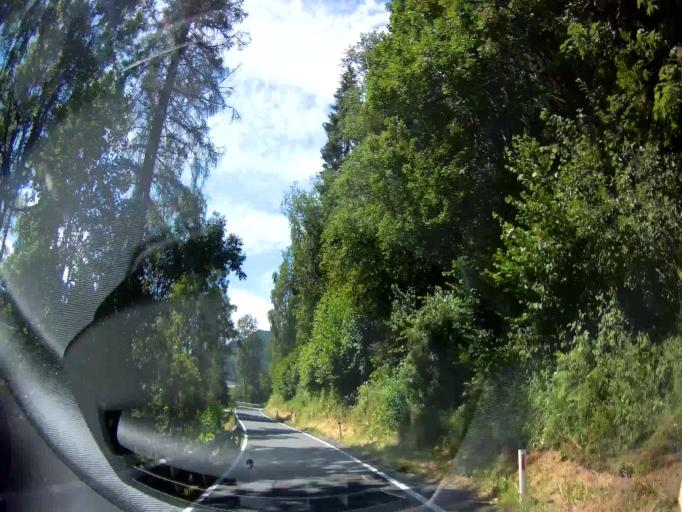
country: AT
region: Carinthia
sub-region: Politischer Bezirk Sankt Veit an der Glan
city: Glodnitz
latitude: 46.9096
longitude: 14.0944
